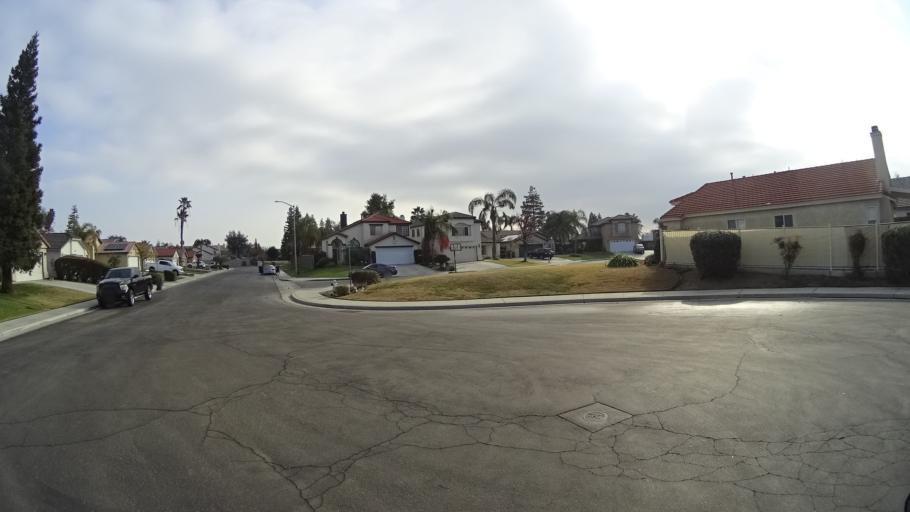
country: US
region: California
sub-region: Kern County
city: Greenfield
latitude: 35.3044
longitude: -119.0741
